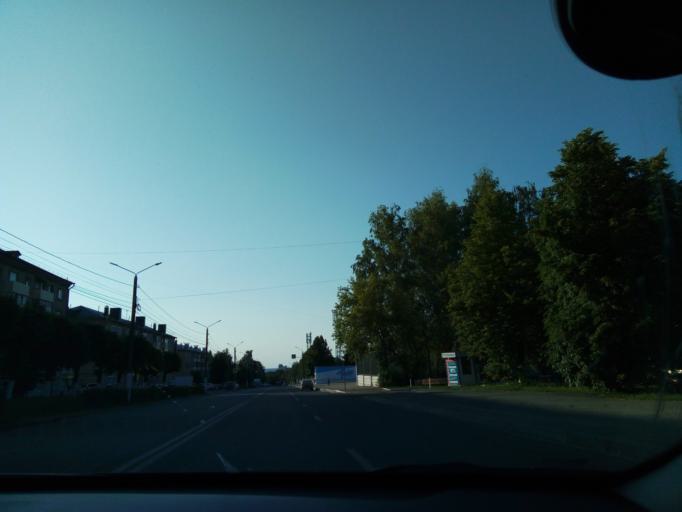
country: RU
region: Chuvashia
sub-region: Cheboksarskiy Rayon
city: Cheboksary
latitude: 56.1212
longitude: 47.2652
